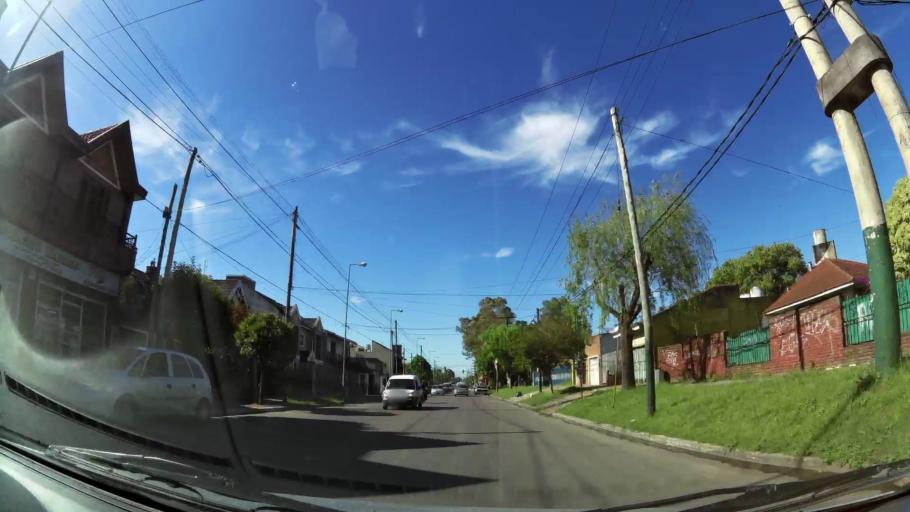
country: AR
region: Buenos Aires
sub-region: Partido de Lomas de Zamora
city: Lomas de Zamora
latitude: -34.7646
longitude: -58.4231
